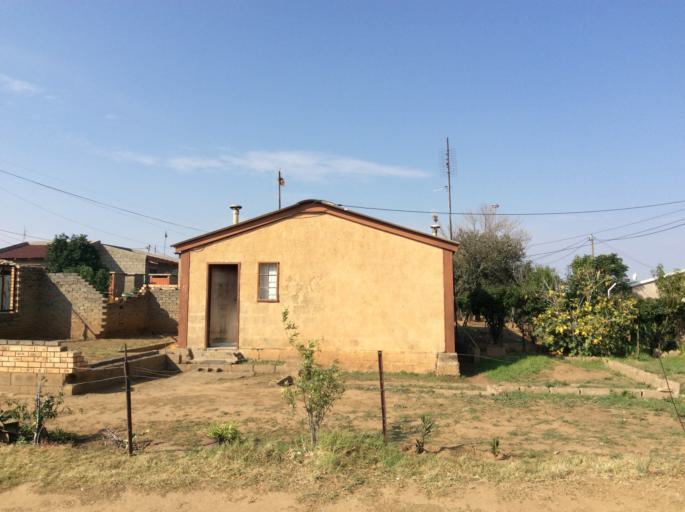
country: LS
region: Mafeteng
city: Mafeteng
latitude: -29.7162
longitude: 27.0285
